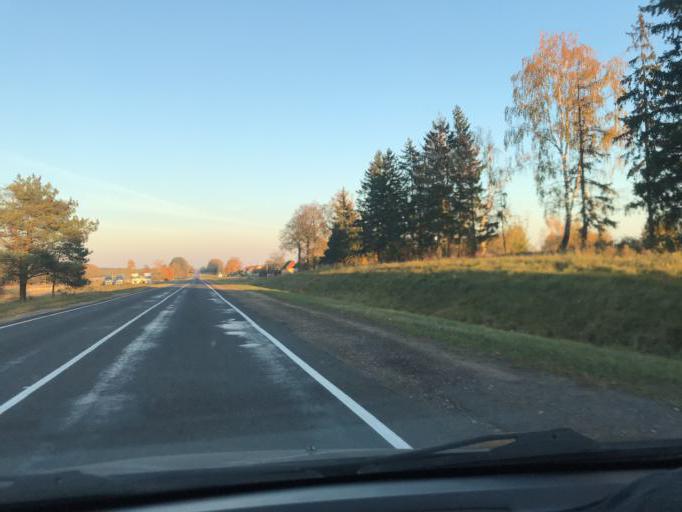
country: BY
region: Minsk
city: Staryya Darohi
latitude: 53.0595
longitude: 28.4739
